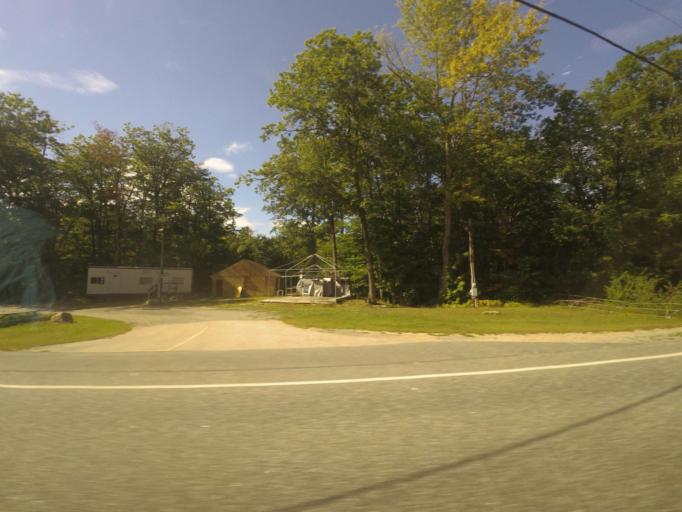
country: US
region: New Hampshire
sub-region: Hillsborough County
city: Antrim
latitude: 43.0749
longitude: -72.0159
